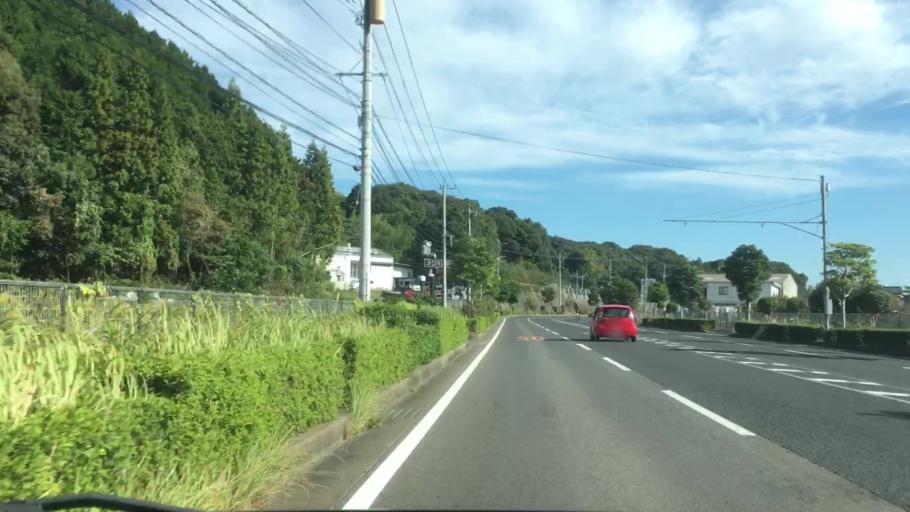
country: JP
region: Nagasaki
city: Sasebo
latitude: 33.1119
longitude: 129.7869
